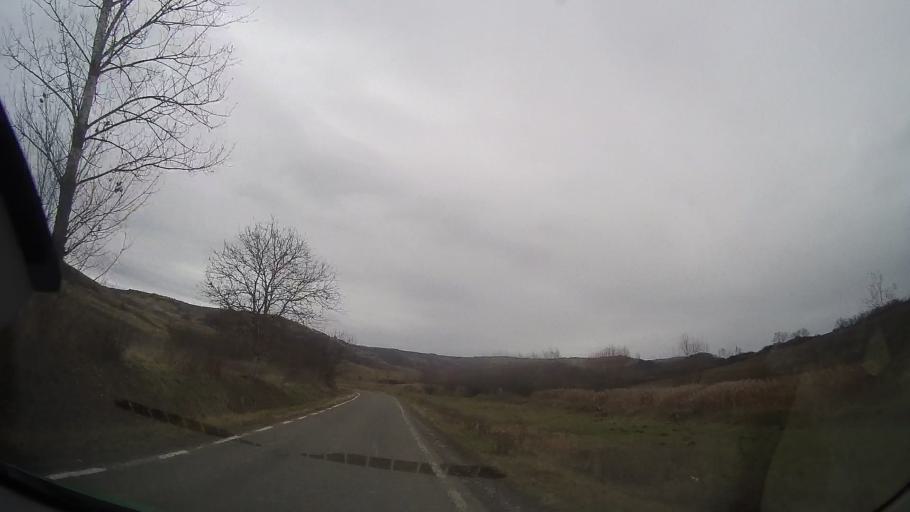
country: RO
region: Mures
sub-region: Comuna Bala
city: Bala
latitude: 46.7166
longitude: 24.5422
